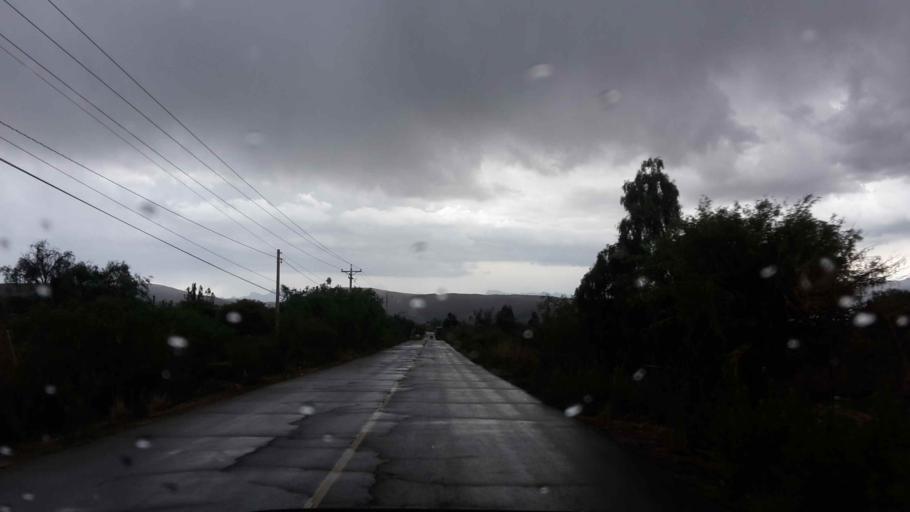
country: BO
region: Cochabamba
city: Tarata
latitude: -17.5664
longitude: -66.0773
